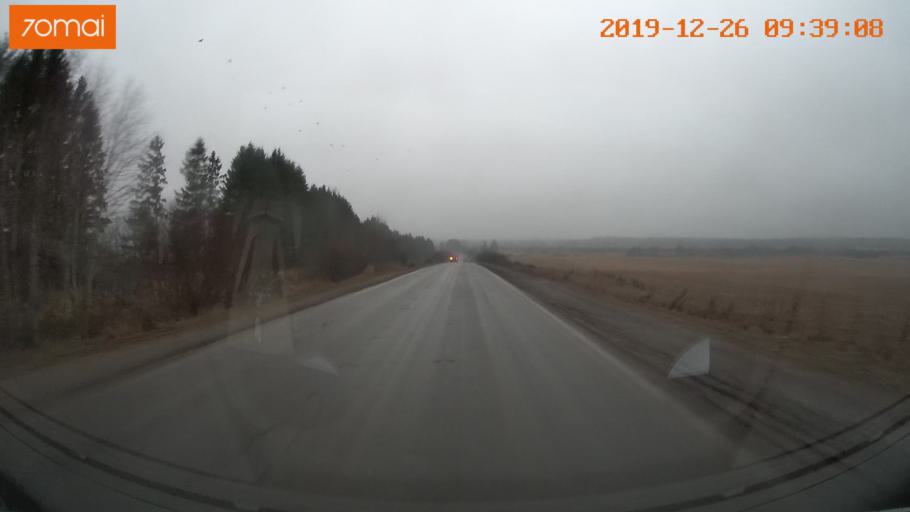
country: RU
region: Vologda
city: Vologda
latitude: 59.1514
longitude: 40.0305
